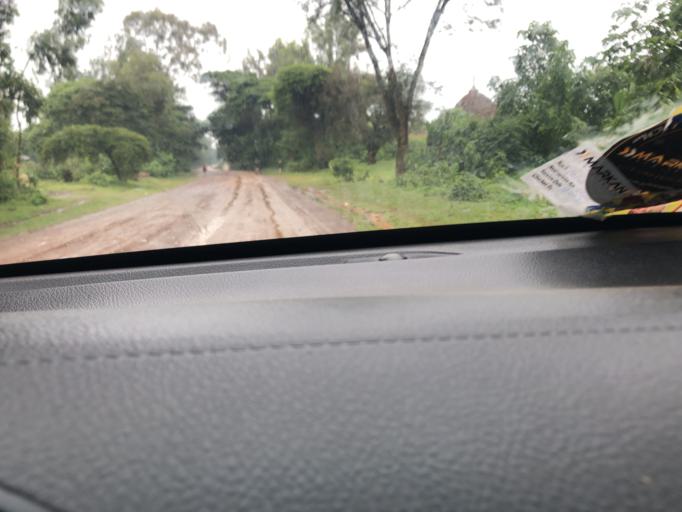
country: ET
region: Southern Nations, Nationalities, and People's Region
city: Butajira
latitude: 7.8654
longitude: 38.1739
